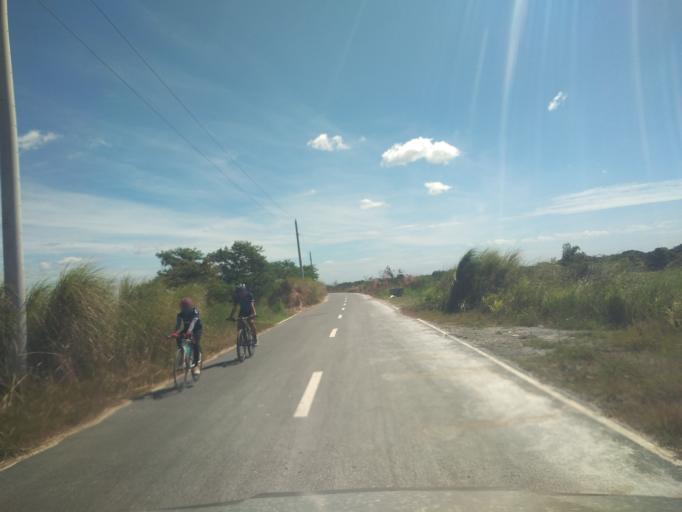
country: PH
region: Central Luzon
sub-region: Province of Pampanga
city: Balas
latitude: 15.0541
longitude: 120.5752
